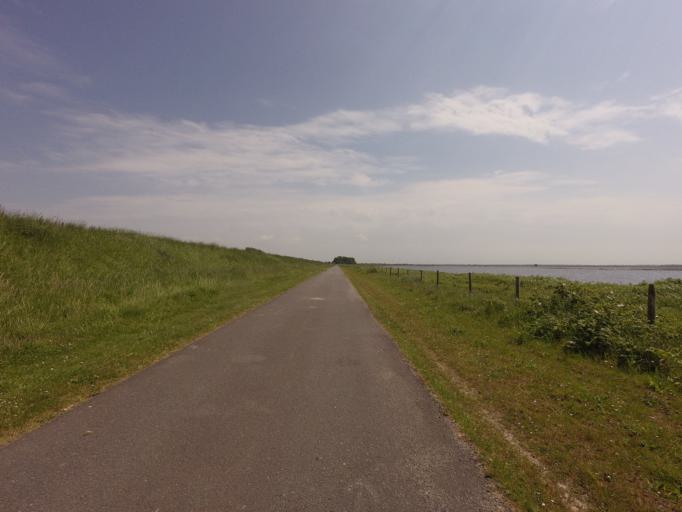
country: NL
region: South Holland
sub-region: Gemeente Spijkenisse
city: Spijkenisse
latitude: 51.7418
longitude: 4.3276
